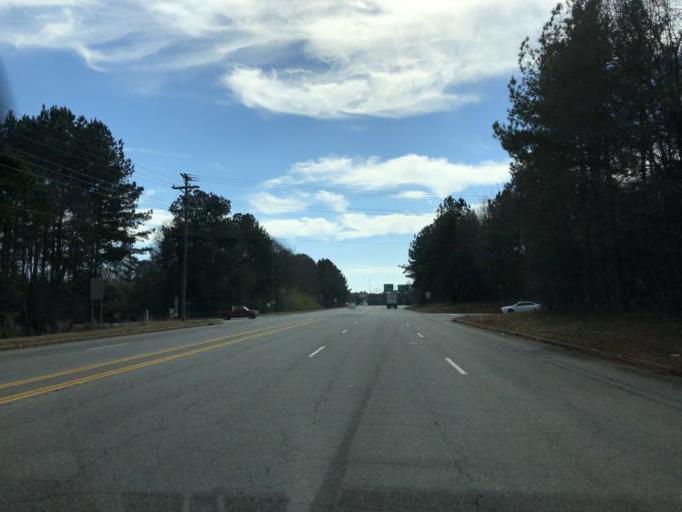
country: US
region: South Carolina
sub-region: Spartanburg County
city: Mayo
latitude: 35.0310
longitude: -81.8778
